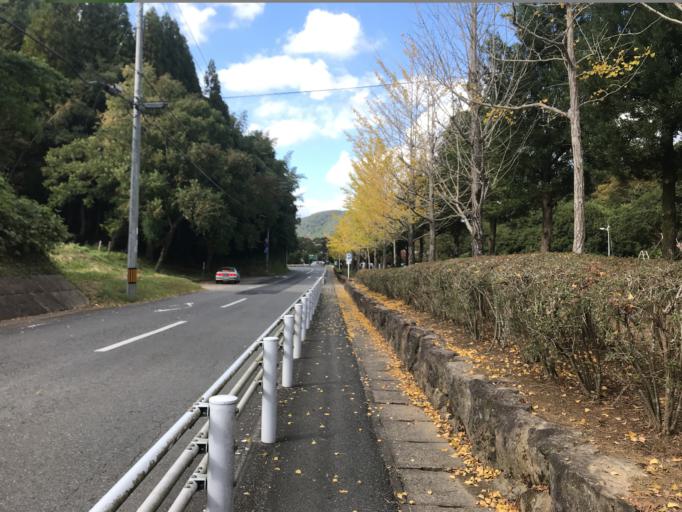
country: JP
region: Saga Prefecture
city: Takeocho-takeo
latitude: 33.1884
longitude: 130.0273
